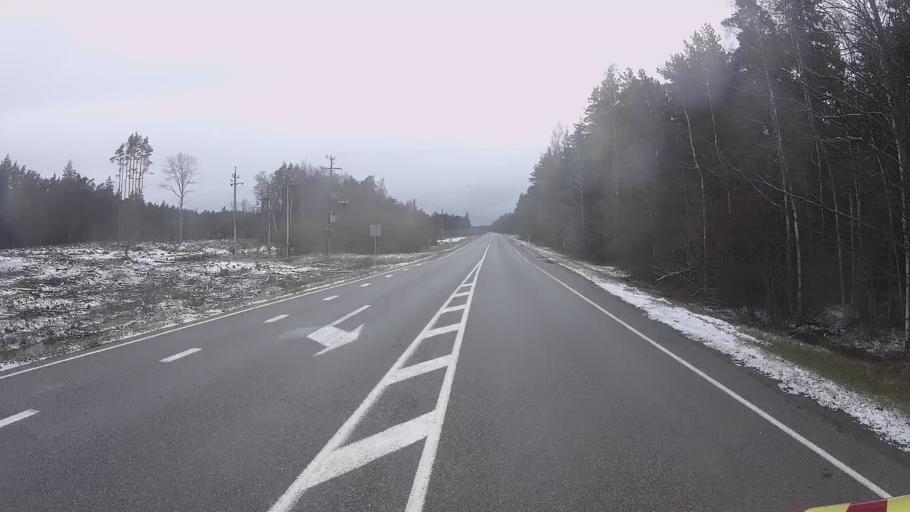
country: EE
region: Hiiumaa
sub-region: Kaerdla linn
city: Kardla
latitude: 59.0112
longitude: 22.6715
